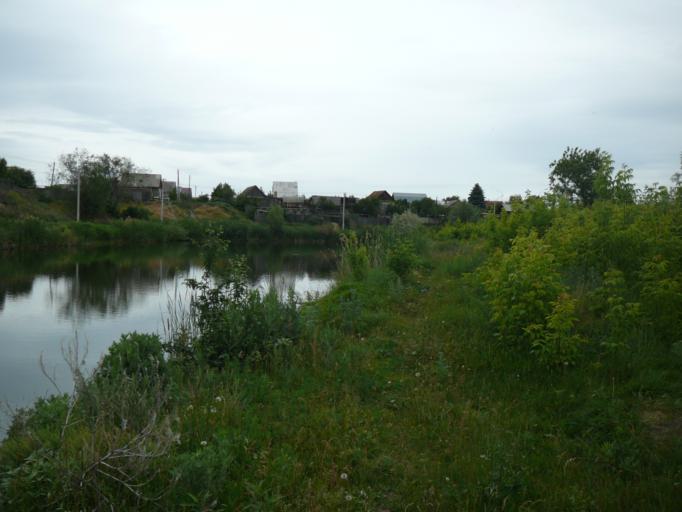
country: RU
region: Saratov
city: Engel's
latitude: 51.4736
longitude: 46.0918
